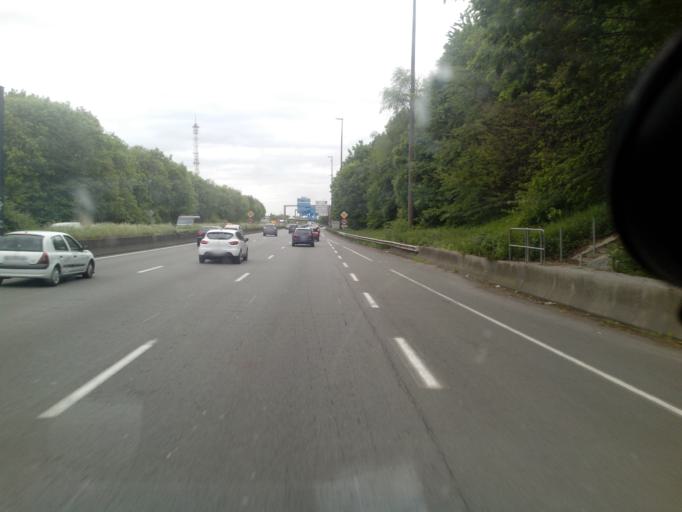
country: FR
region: Nord-Pas-de-Calais
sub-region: Departement du Nord
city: Mons-en-Baroeul
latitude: 50.6502
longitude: 3.1012
